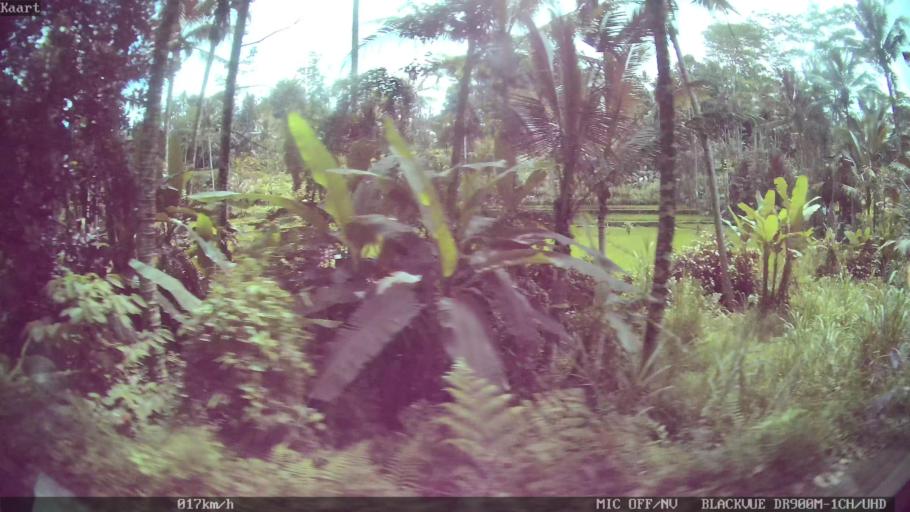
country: ID
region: Bali
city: Banjar Susut Kaja
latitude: -8.4409
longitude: 115.3319
